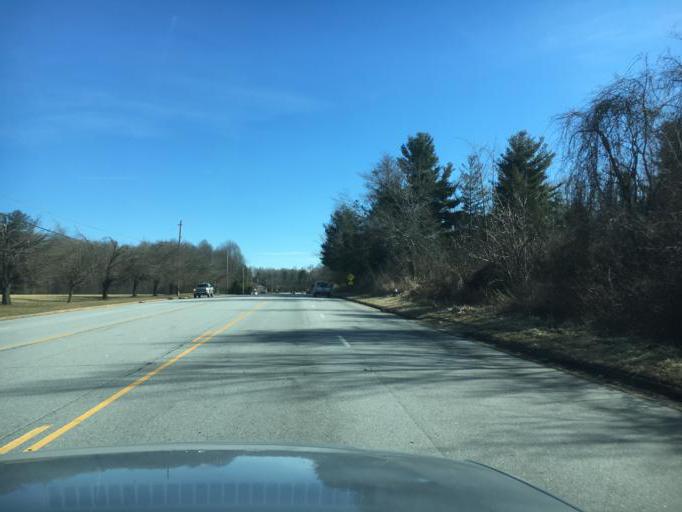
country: US
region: North Carolina
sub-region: Henderson County
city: East Flat Rock
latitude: 35.2712
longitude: -82.4127
